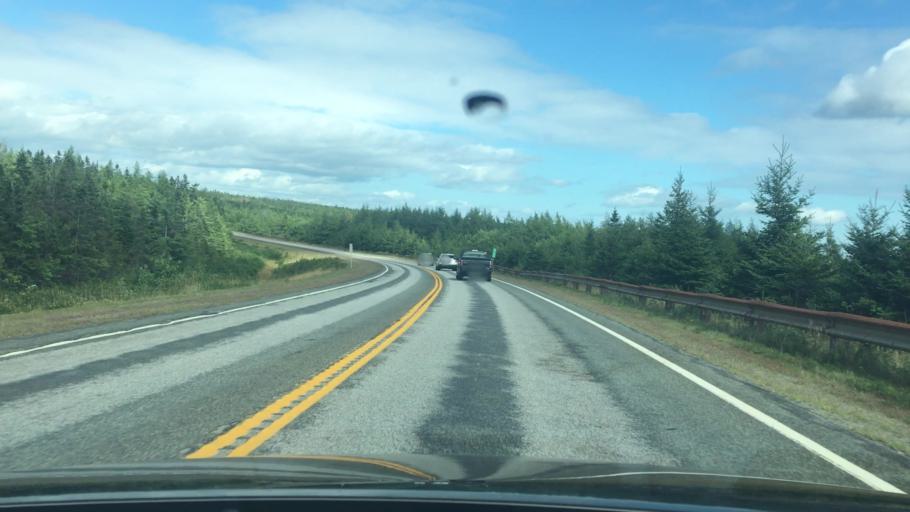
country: CA
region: Nova Scotia
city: Princeville
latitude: 45.6121
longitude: -61.0604
